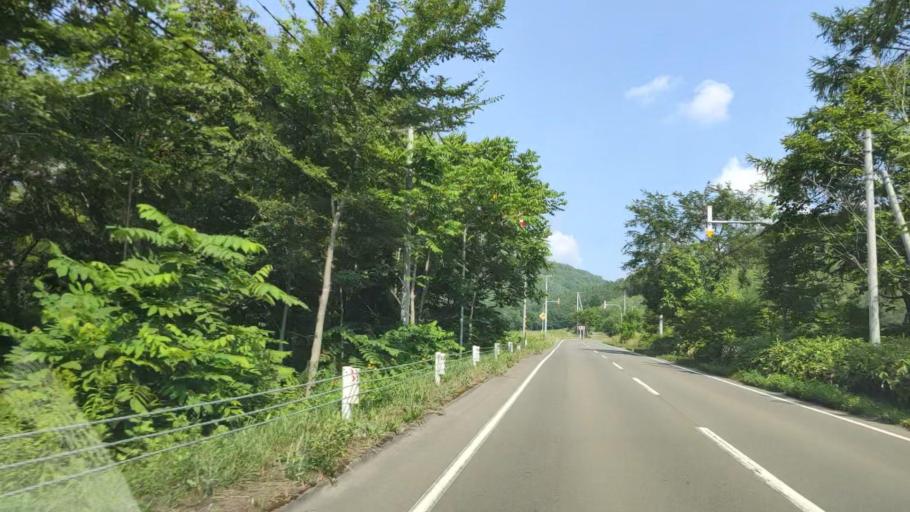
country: JP
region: Hokkaido
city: Shimo-furano
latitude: 43.4237
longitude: 142.4004
